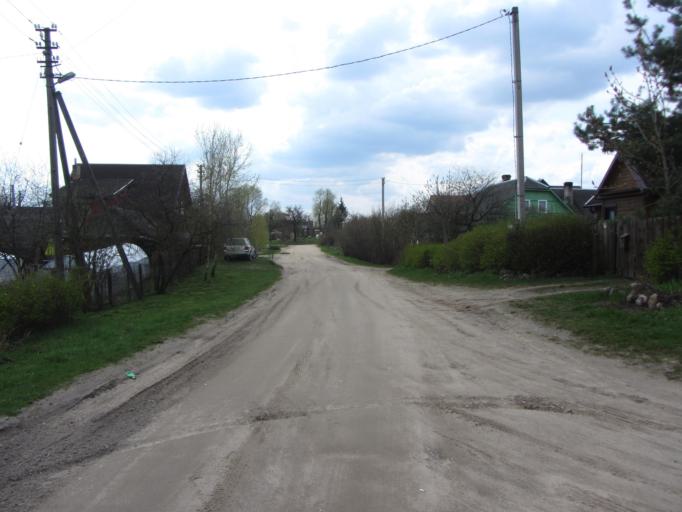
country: LT
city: Lentvaris
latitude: 54.6455
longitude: 25.0681
